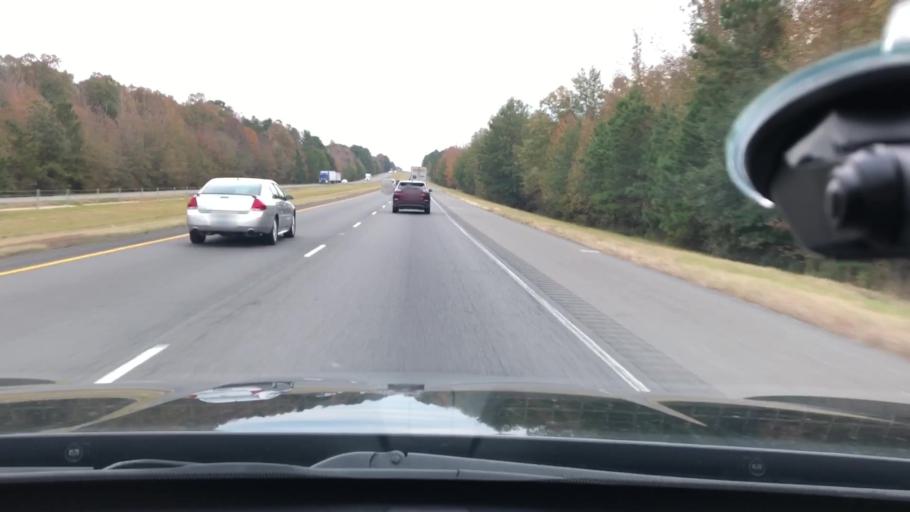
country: US
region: Arkansas
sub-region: Clark County
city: Arkadelphia
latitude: 34.0502
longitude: -93.1343
